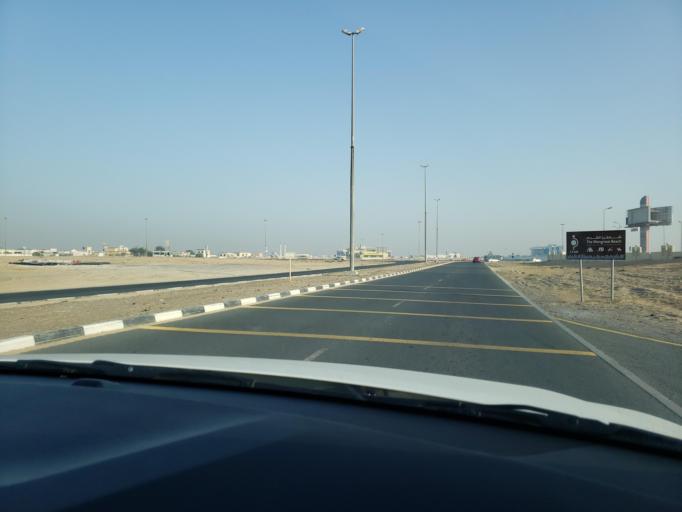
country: AE
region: Umm al Qaywayn
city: Umm al Qaywayn
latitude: 25.5061
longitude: 55.5949
